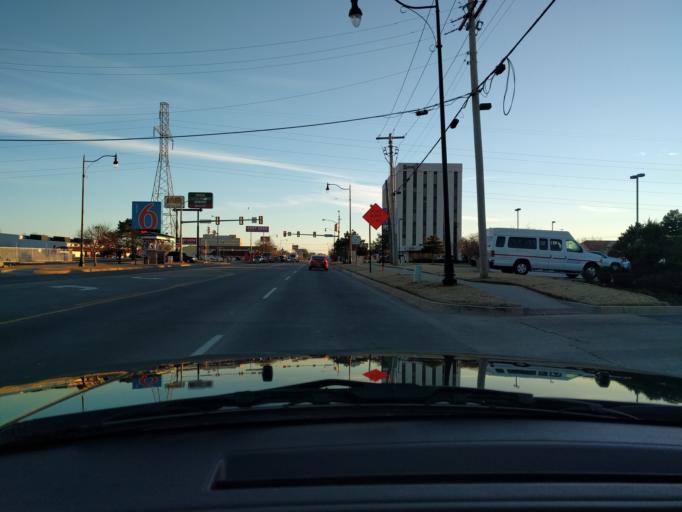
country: US
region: Oklahoma
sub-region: Oklahoma County
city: Warr Acres
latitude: 35.4579
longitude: -97.6012
